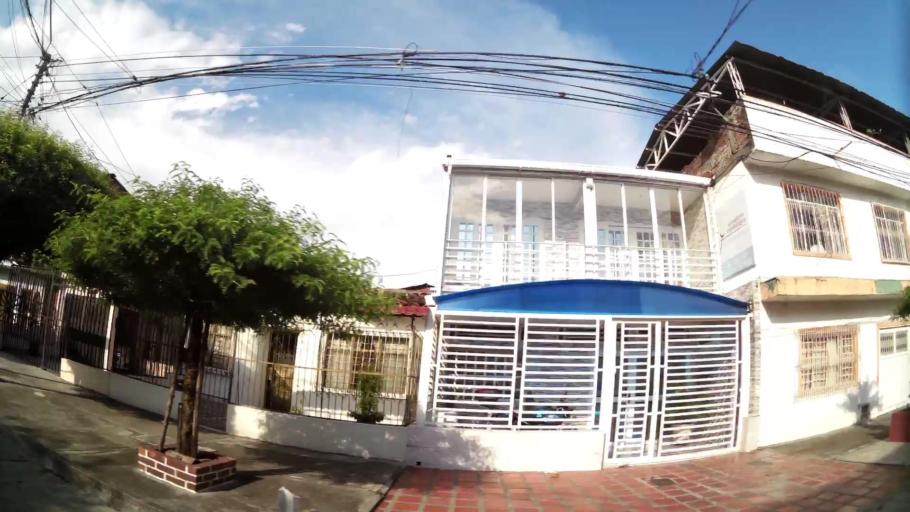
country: CO
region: Valle del Cauca
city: Cali
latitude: 3.4305
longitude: -76.5241
